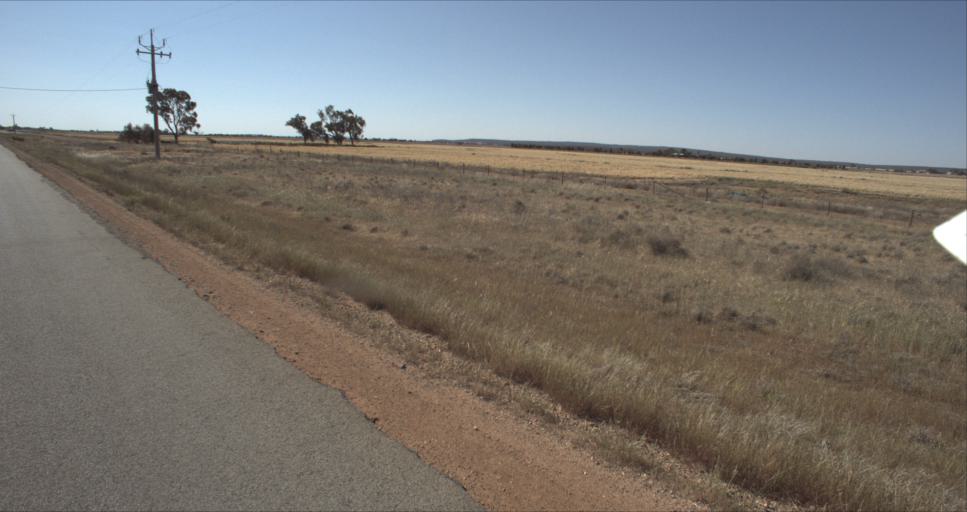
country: AU
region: New South Wales
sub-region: Leeton
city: Leeton
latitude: -34.4976
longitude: 146.3912
